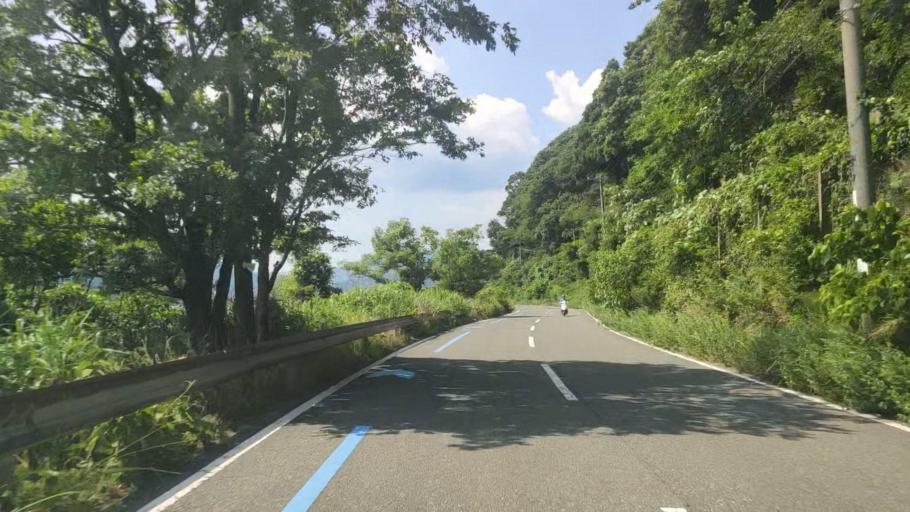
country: JP
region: Shiga Prefecture
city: Nagahama
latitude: 35.5080
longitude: 136.1692
